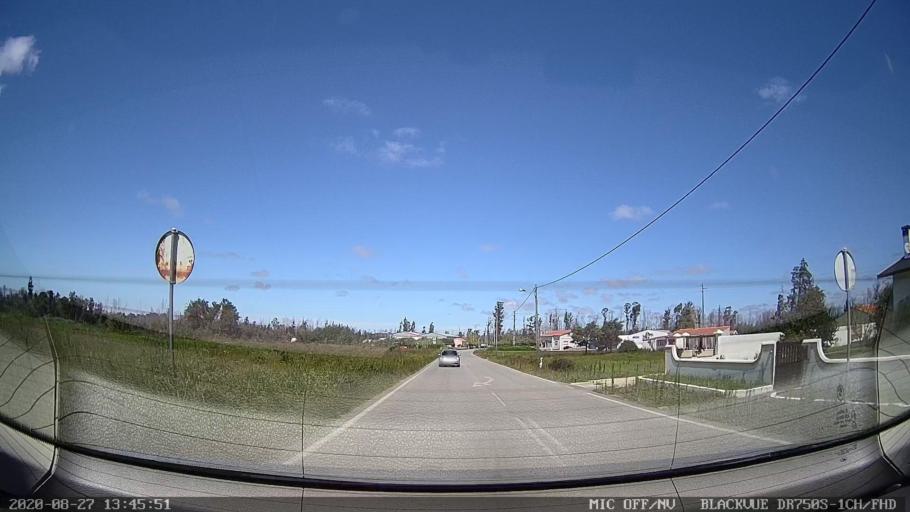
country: PT
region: Coimbra
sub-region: Mira
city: Mira
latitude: 40.4006
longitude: -8.7357
